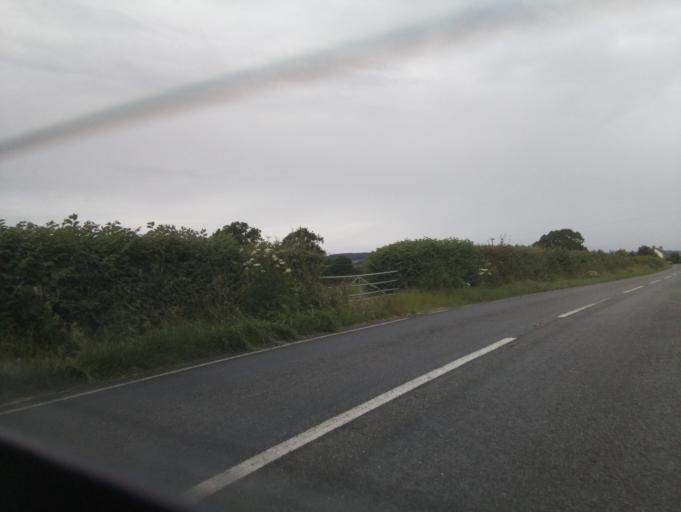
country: GB
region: England
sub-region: Devon
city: Colyton
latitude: 50.7396
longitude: -3.0417
